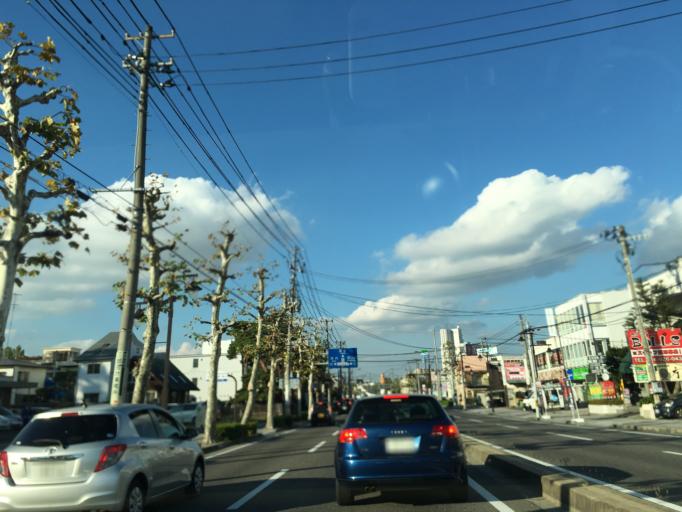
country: JP
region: Fukushima
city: Koriyama
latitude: 37.3979
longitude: 140.3630
